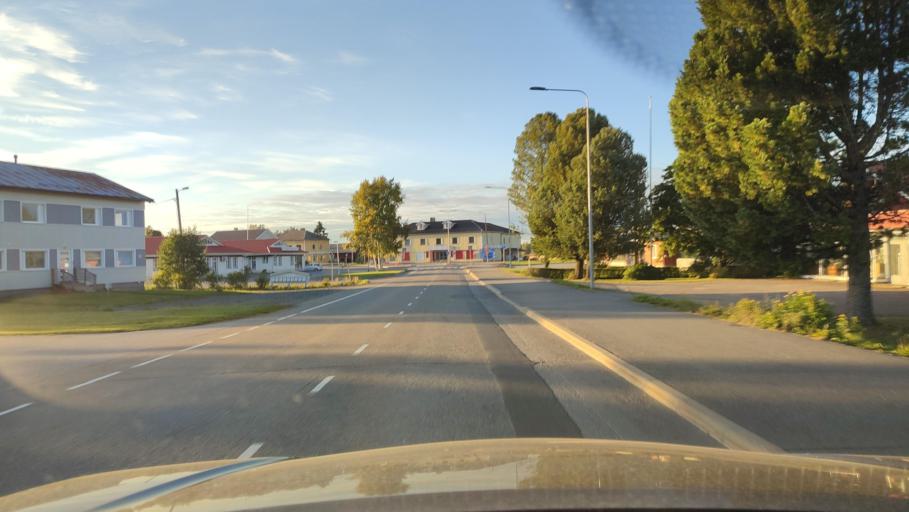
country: FI
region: Ostrobothnia
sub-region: Sydosterbotten
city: Kristinestad
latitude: 62.2536
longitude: 21.5092
